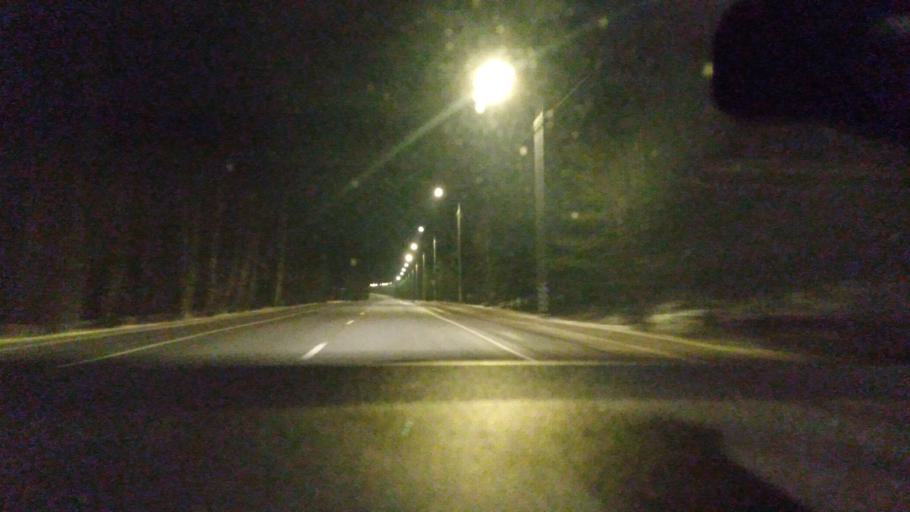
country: RU
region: Moskovskaya
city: Il'inskiy Pogost
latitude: 55.4701
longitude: 38.9631
